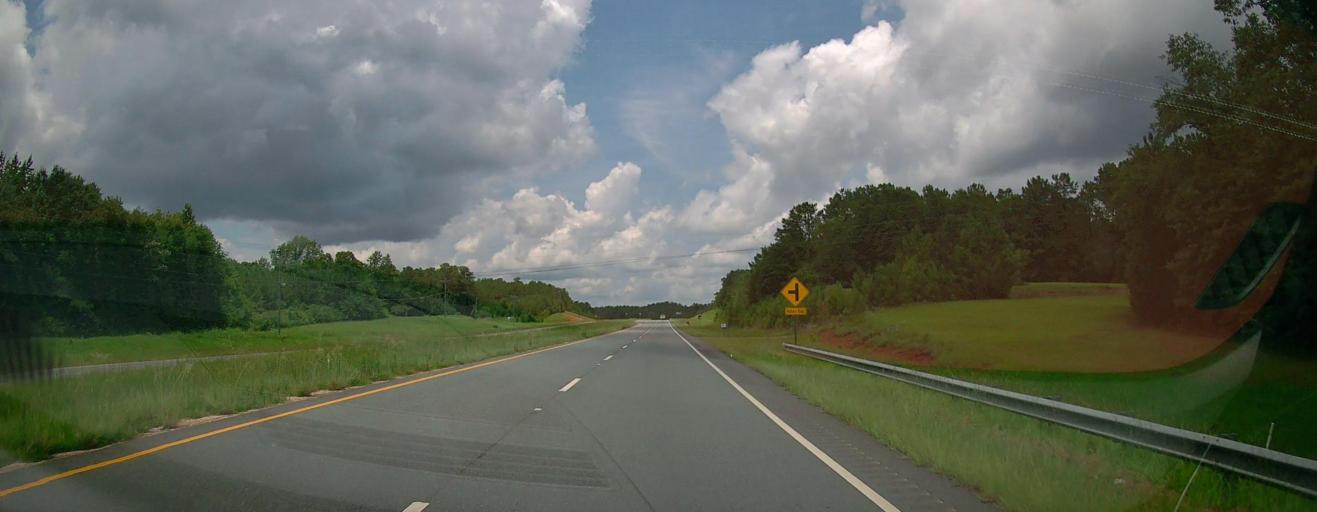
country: US
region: Georgia
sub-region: Upson County
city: Thomaston
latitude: 32.8286
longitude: -84.3076
